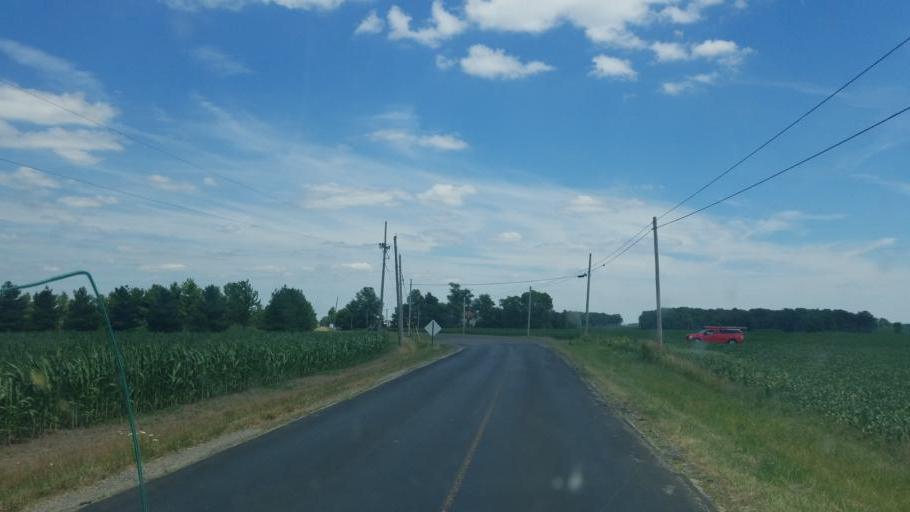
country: US
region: Ohio
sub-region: Williams County
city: Edgerton
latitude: 41.4663
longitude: -84.6921
